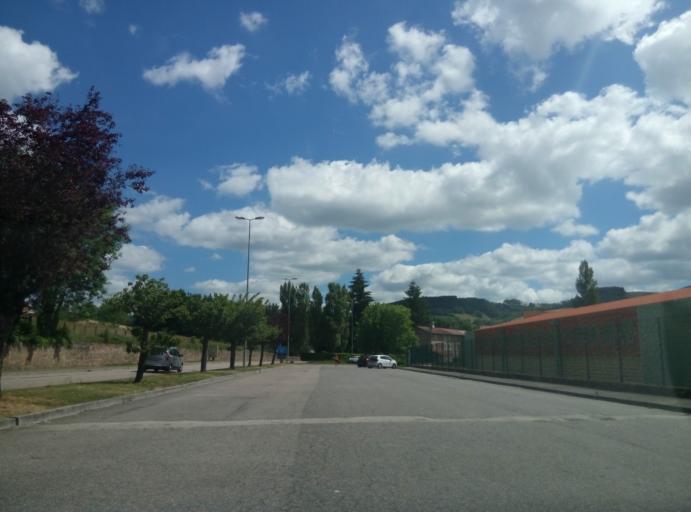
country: FR
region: Rhone-Alpes
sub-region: Departement du Rhone
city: Bourg-de-Thizy
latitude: 46.0386
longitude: 4.2955
